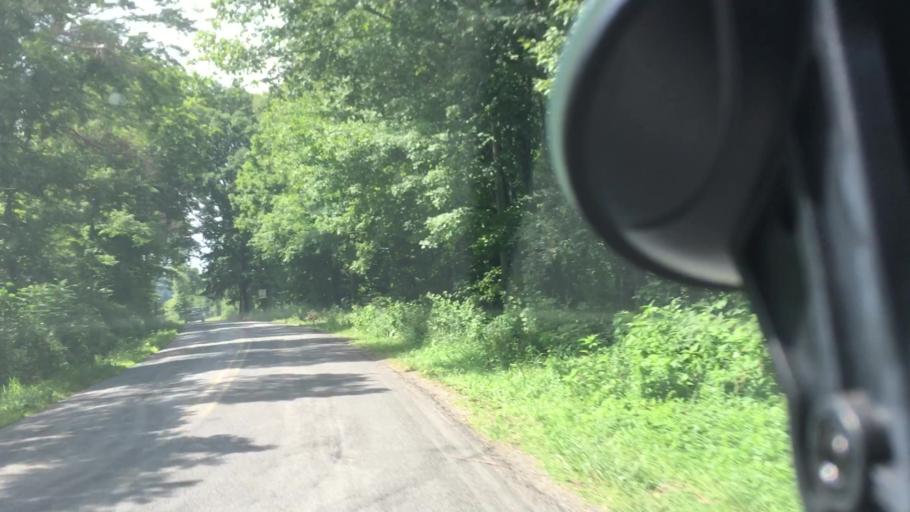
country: US
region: Pennsylvania
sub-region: Mercer County
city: Reynolds Heights
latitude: 41.3019
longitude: -80.3661
